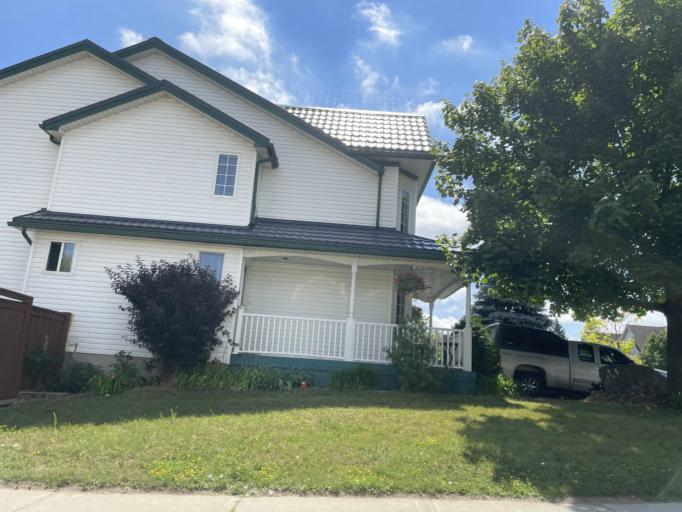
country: CA
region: Ontario
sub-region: Wellington County
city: Guelph
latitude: 43.5132
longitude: -80.2071
